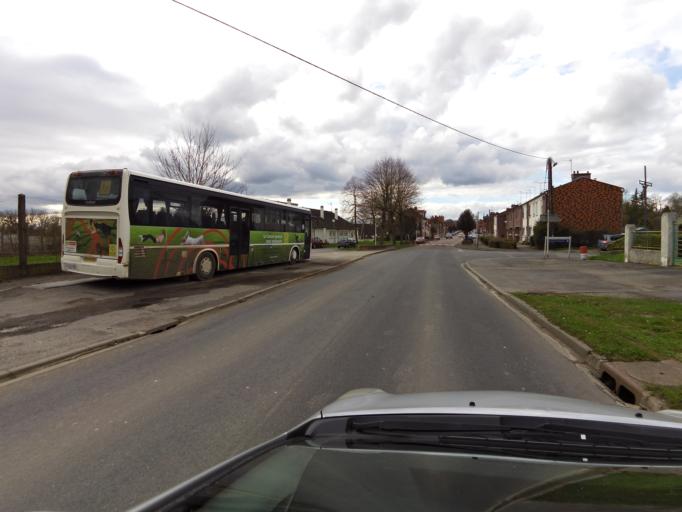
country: FR
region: Picardie
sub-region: Departement de la Somme
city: Roye
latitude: 49.6952
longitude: 2.8001
